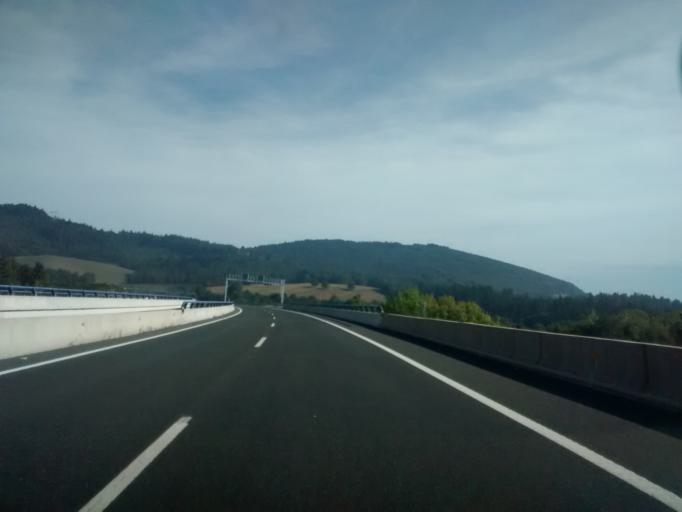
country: ES
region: Basque Country
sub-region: Provincia de Guipuzcoa
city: Leintz-Gatzaga
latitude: 42.9605
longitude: -2.6123
